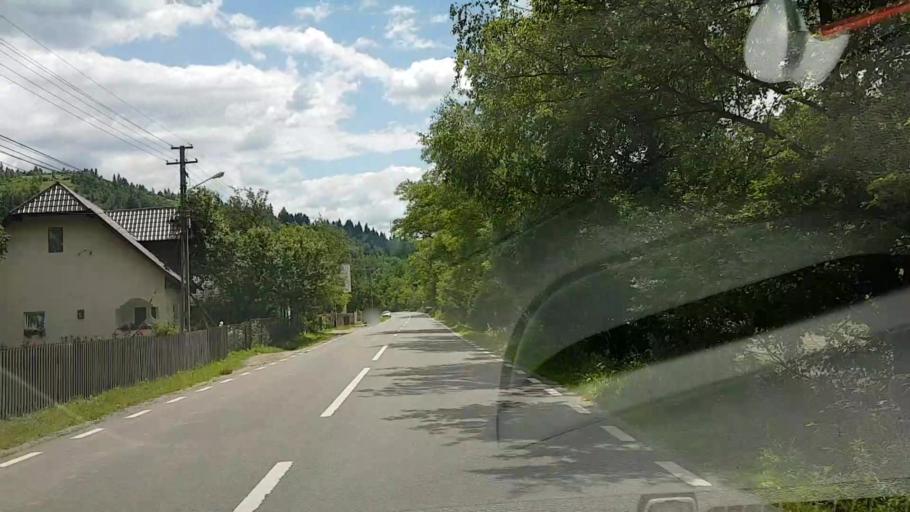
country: RO
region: Suceava
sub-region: Comuna Brosteni
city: Brosteni
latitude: 47.2577
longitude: 25.6910
